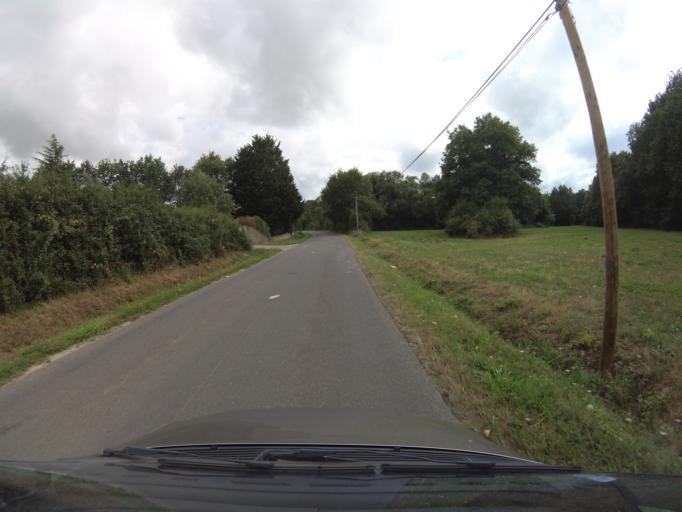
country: FR
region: Pays de la Loire
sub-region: Departement de la Loire-Atlantique
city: La Limouziniere
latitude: 47.0246
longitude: -1.5706
